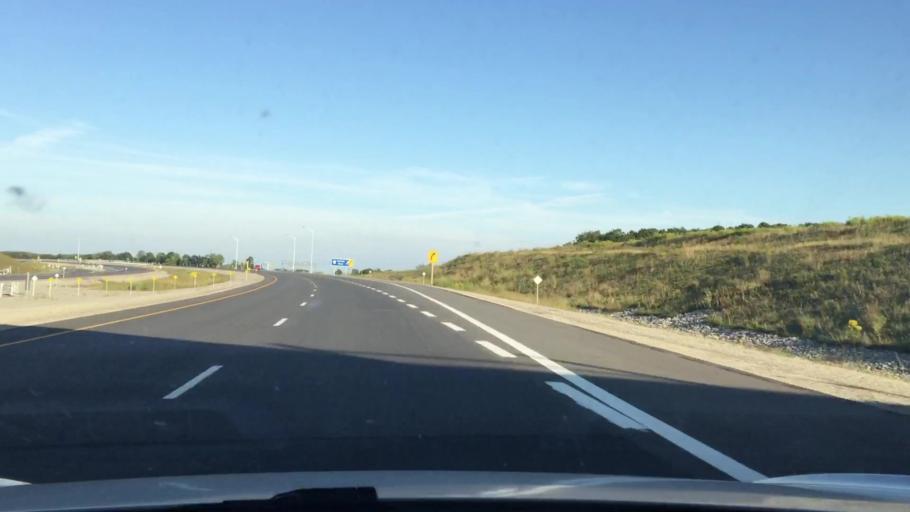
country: CA
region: Ontario
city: Oshawa
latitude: 43.9650
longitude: -78.8204
